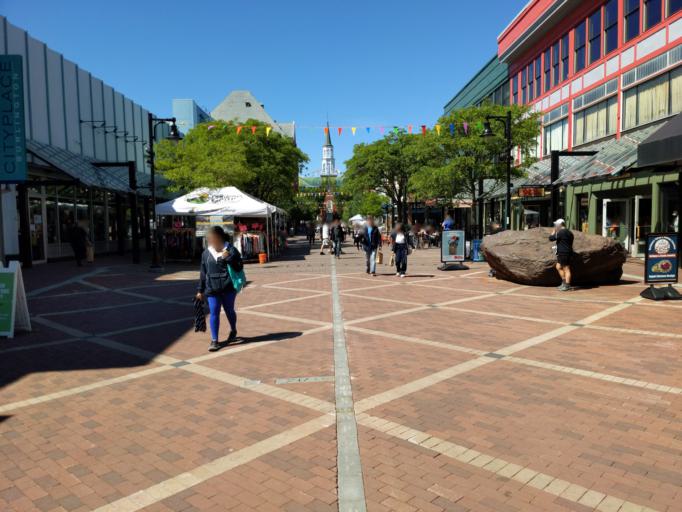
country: US
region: Vermont
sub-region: Chittenden County
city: Burlington
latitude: 44.4788
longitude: -73.2127
